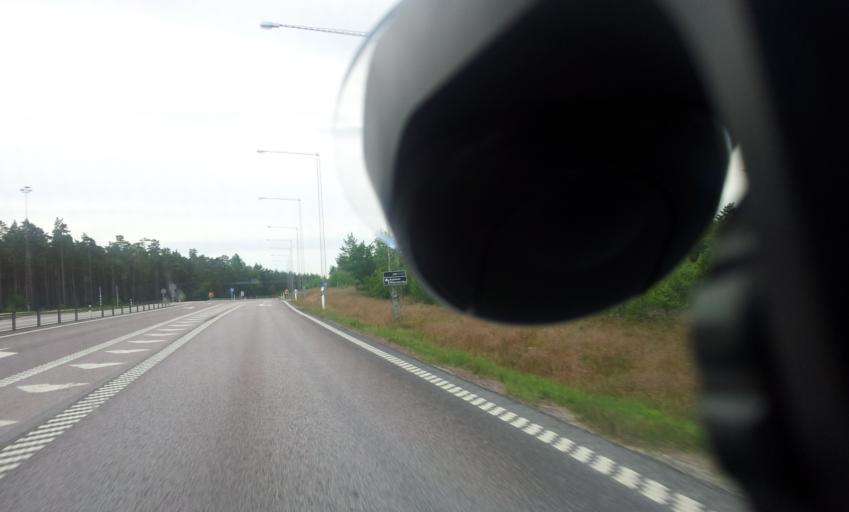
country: SE
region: Kalmar
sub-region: Monsteras Kommun
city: Moensteras
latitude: 57.0820
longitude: 16.4836
